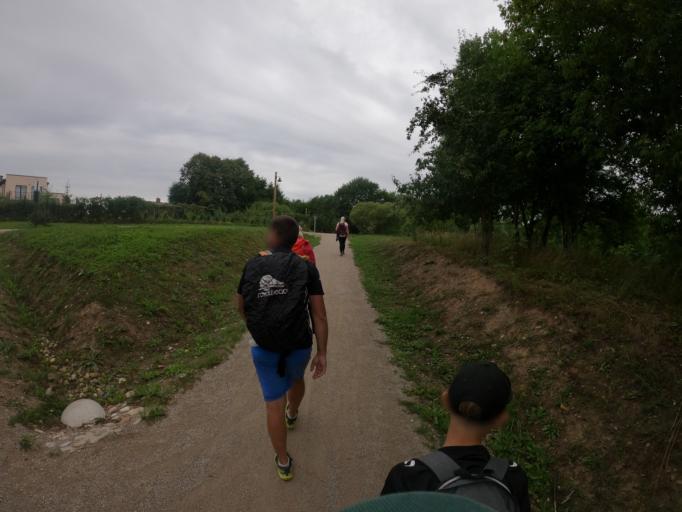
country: LV
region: Kuldigas Rajons
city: Kuldiga
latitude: 56.9668
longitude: 21.9913
